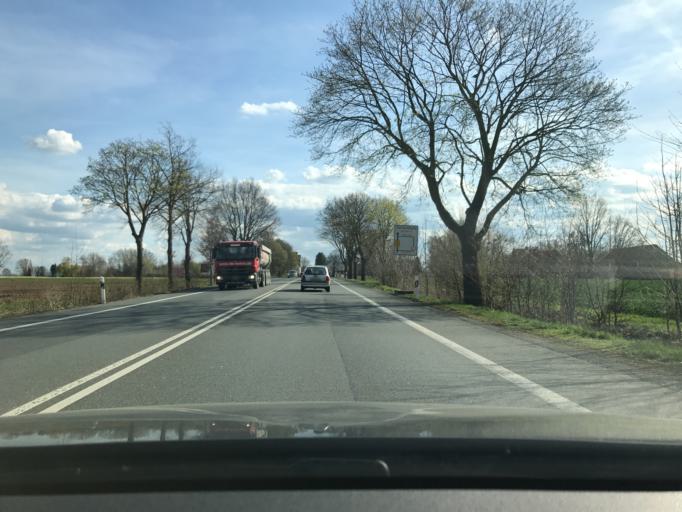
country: DE
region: North Rhine-Westphalia
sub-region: Regierungsbezirk Arnsberg
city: Werl
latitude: 51.5994
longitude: 7.8551
